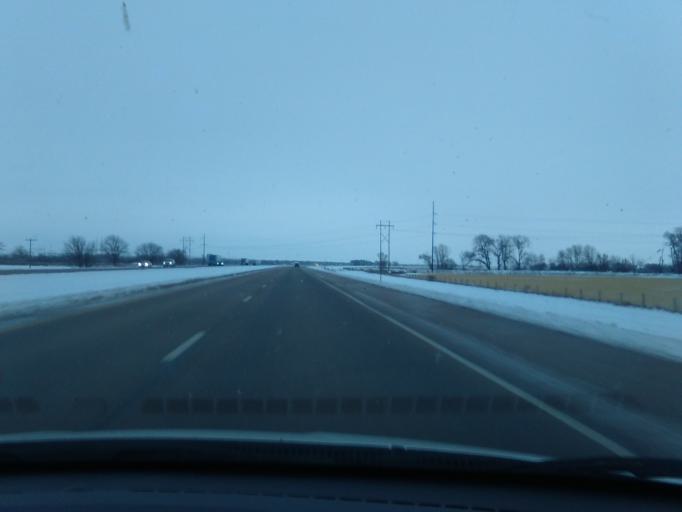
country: US
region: Nebraska
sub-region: Keith County
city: Ogallala
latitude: 41.1172
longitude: -101.6951
